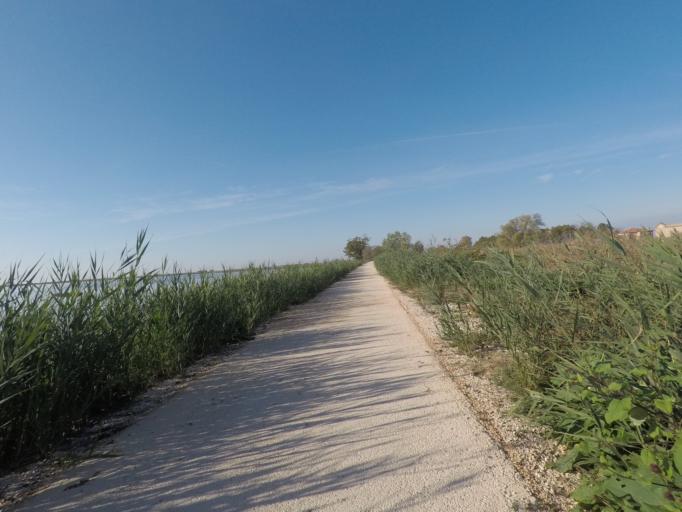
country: IT
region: Veneto
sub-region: Provincia di Venezia
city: Musile di Piave
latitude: 45.5699
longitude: 12.5090
